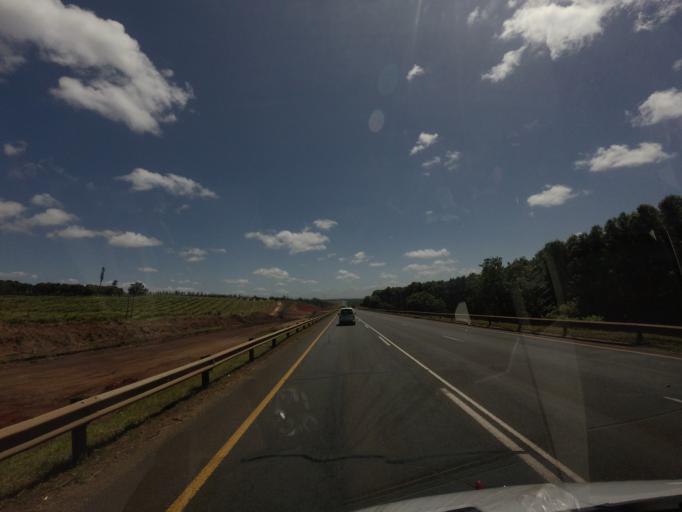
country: ZA
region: KwaZulu-Natal
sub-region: uThungulu District Municipality
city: Empangeni
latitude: -28.7951
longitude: 31.9219
